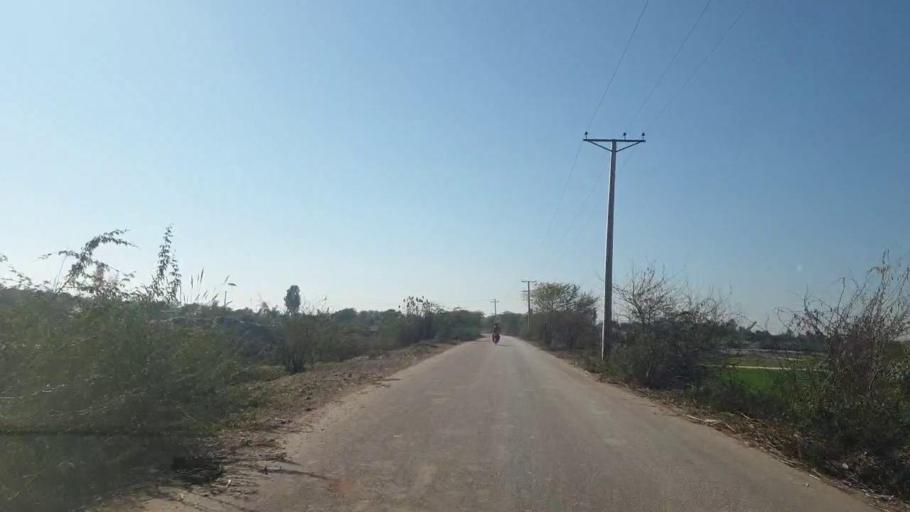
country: PK
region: Sindh
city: Kot Diji
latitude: 27.2987
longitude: 68.6418
